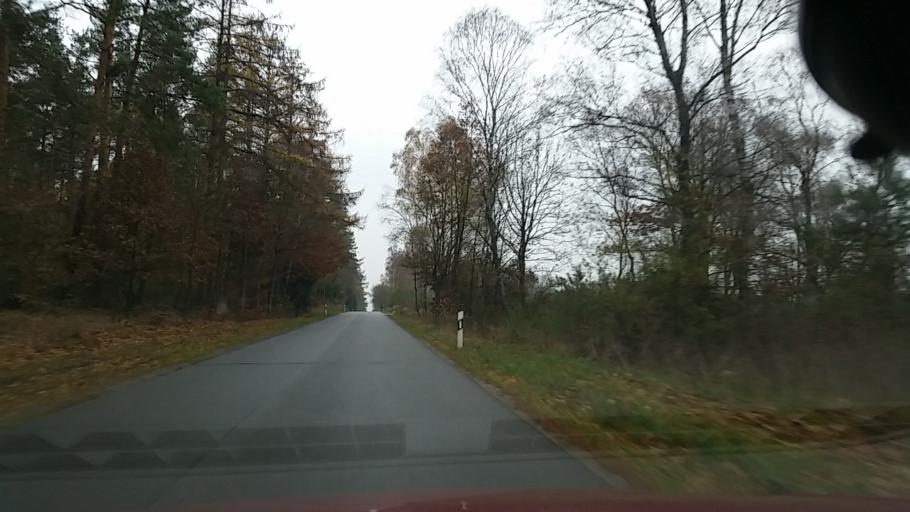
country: DE
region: Lower Saxony
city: Obernholz
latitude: 52.7908
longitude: 10.5638
